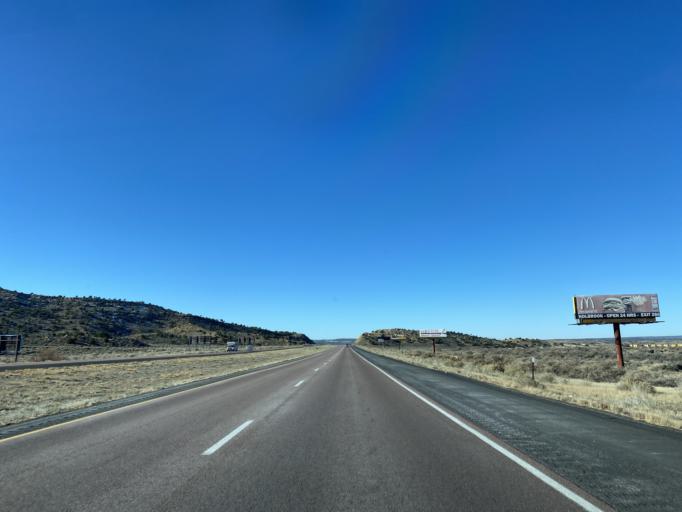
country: US
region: New Mexico
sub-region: McKinley County
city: Gallup
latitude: 35.4925
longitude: -108.8787
